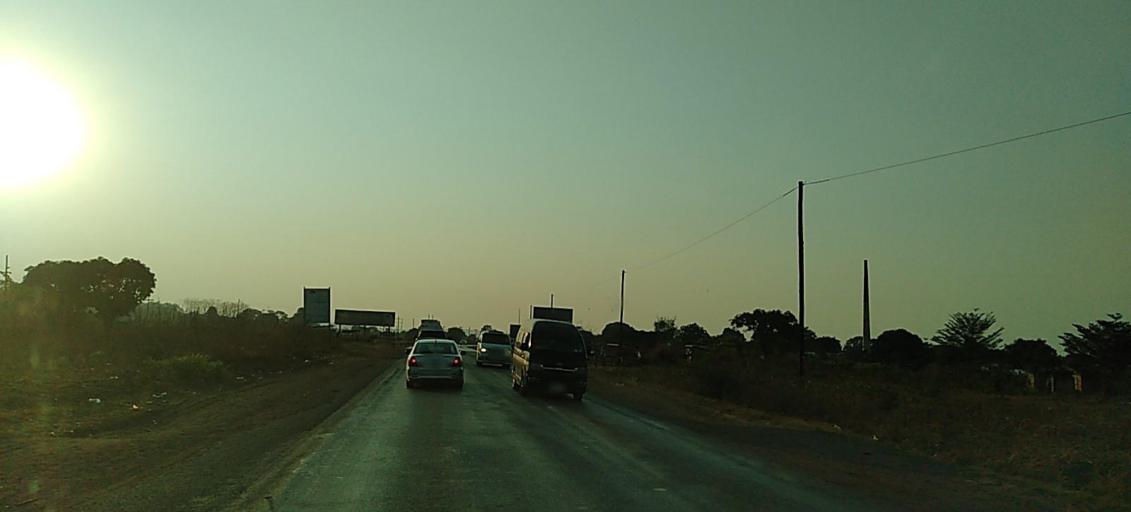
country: ZM
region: Copperbelt
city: Ndola
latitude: -13.0319
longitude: 28.6861
